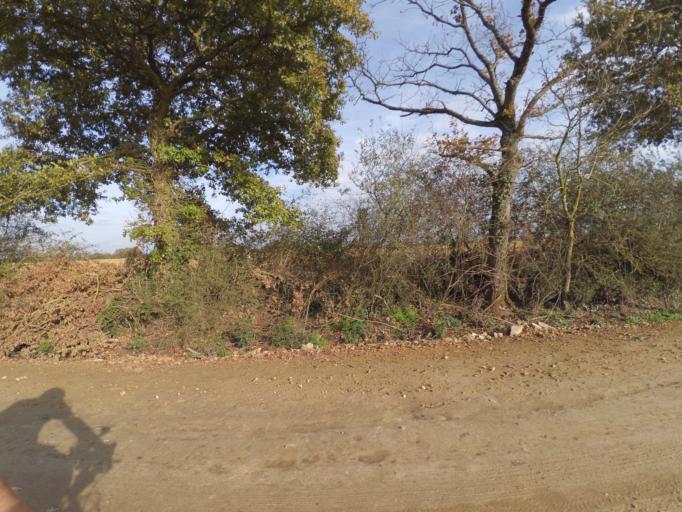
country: FR
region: Pays de la Loire
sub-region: Departement de la Vendee
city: Saint-Hilaire-de-Loulay
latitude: 47.0061
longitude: -1.3623
